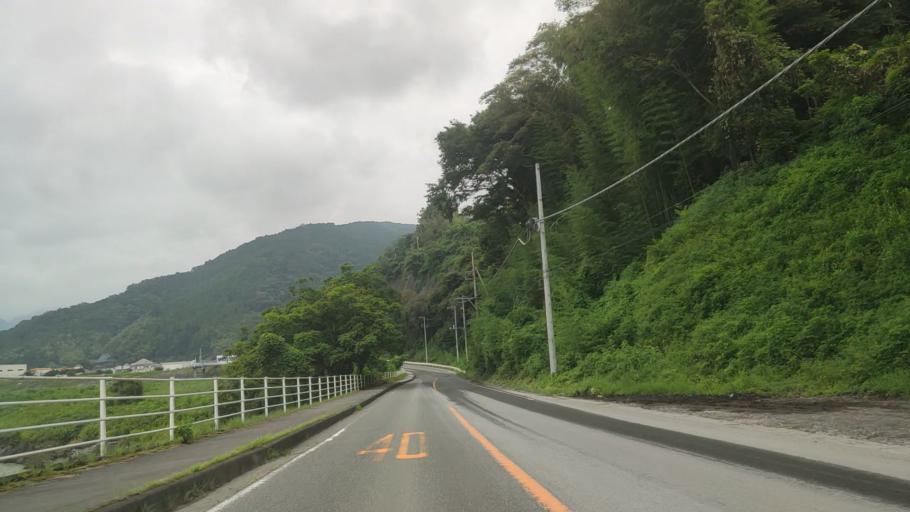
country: JP
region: Shizuoka
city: Fujinomiya
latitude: 35.2044
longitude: 138.5550
